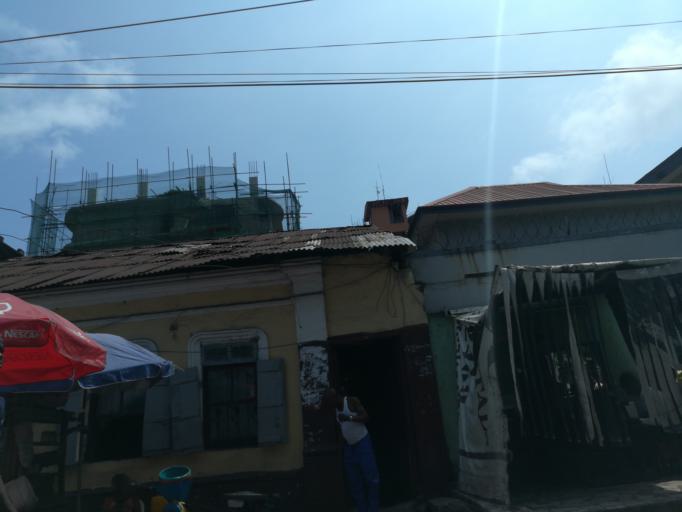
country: NG
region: Lagos
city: Lagos
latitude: 6.4510
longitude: 3.3941
